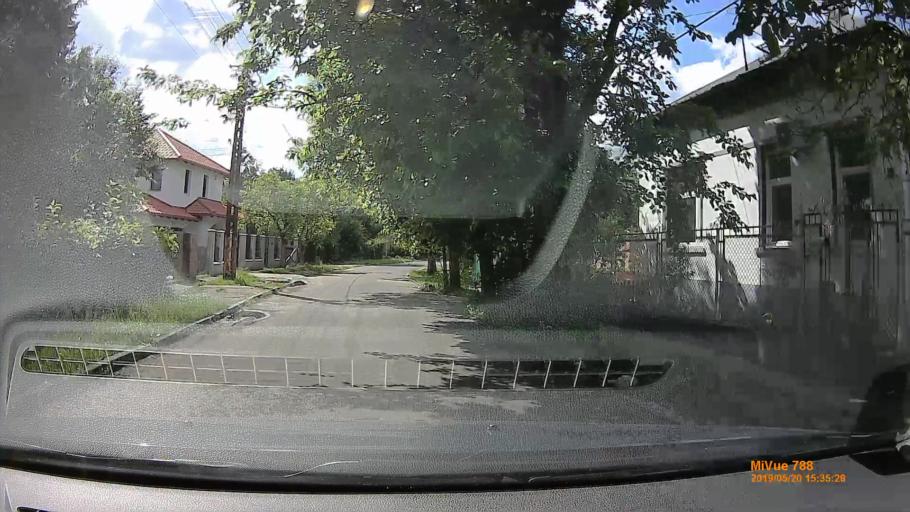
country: HU
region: Budapest
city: Budapest XVII. keruelet
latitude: 47.4896
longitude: 19.2531
